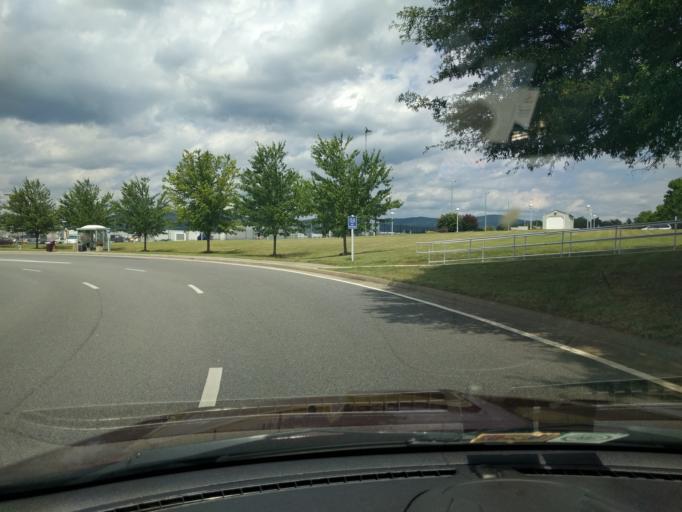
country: US
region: Virginia
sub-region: Roanoke County
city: Hollins
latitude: 37.3204
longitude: -79.9688
